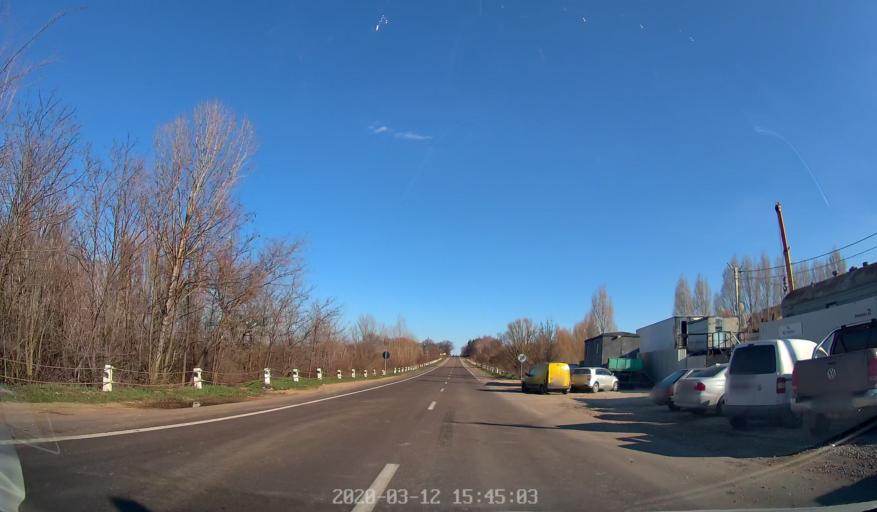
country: MD
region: Chisinau
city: Stauceni
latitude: 47.1081
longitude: 28.8693
